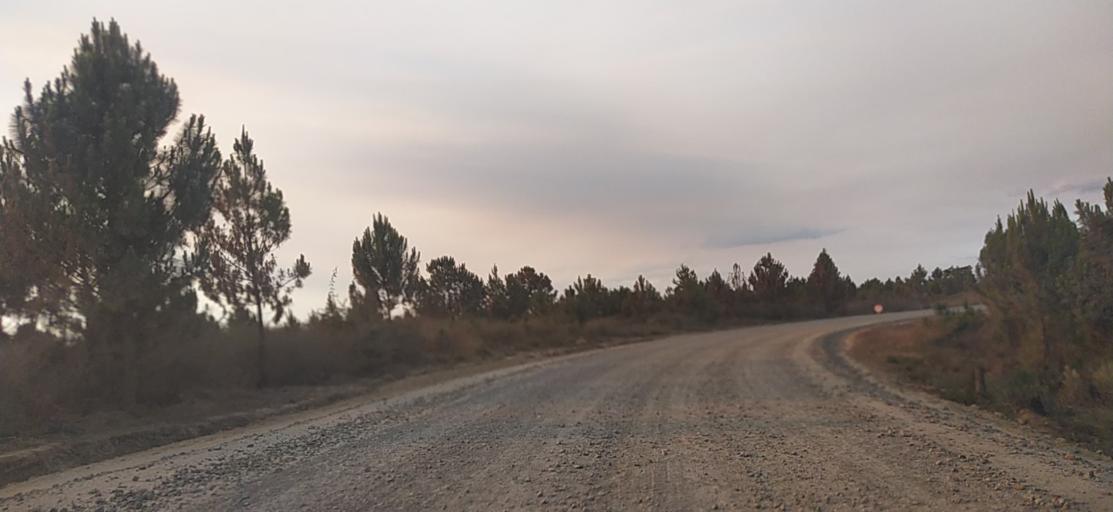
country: MG
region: Analamanga
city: Anjozorobe
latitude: -18.5088
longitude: 48.2620
